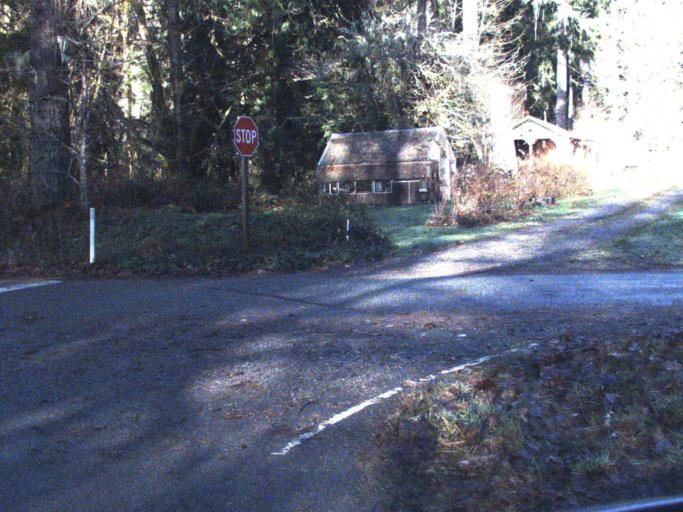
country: US
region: Washington
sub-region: Snohomish County
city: Darrington
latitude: 48.4919
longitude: -121.5594
